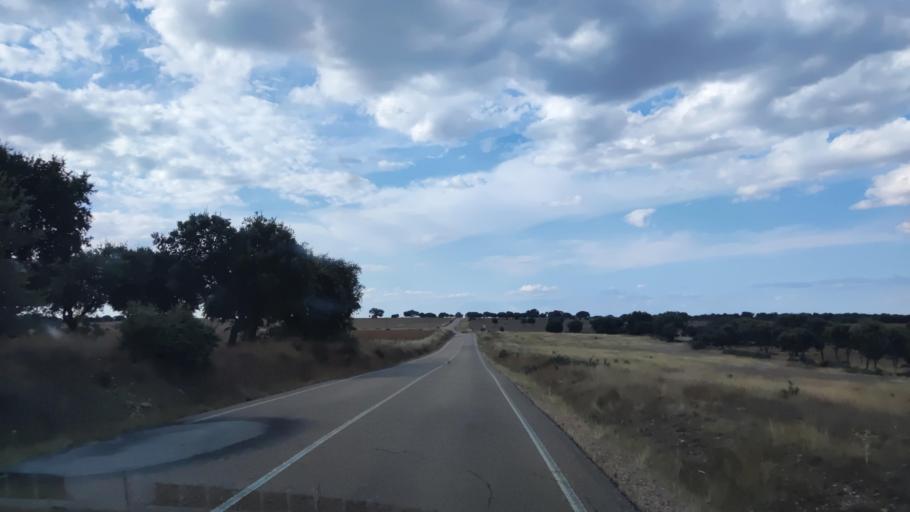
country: ES
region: Castille and Leon
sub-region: Provincia de Salamanca
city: Martiago
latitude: 40.4783
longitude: -6.4910
